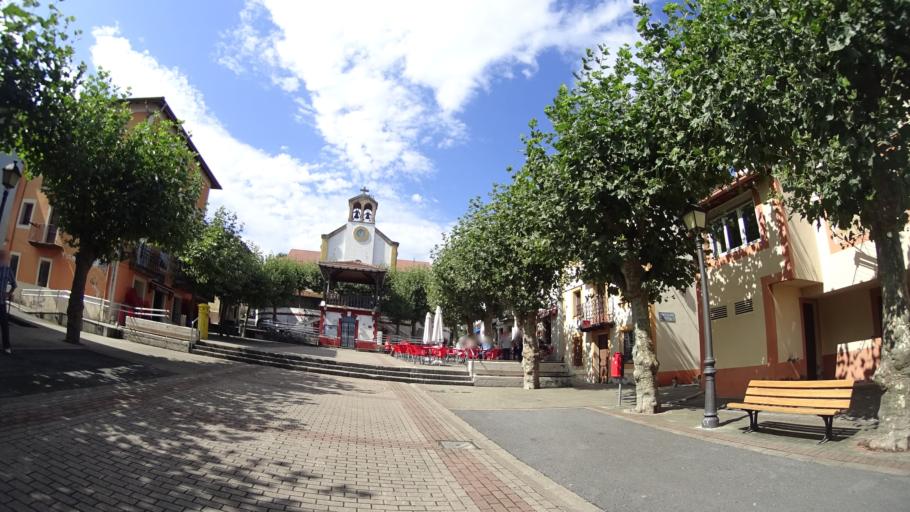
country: ES
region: Basque Country
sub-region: Bizkaia
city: Urtuella
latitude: 43.2846
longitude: -3.0542
